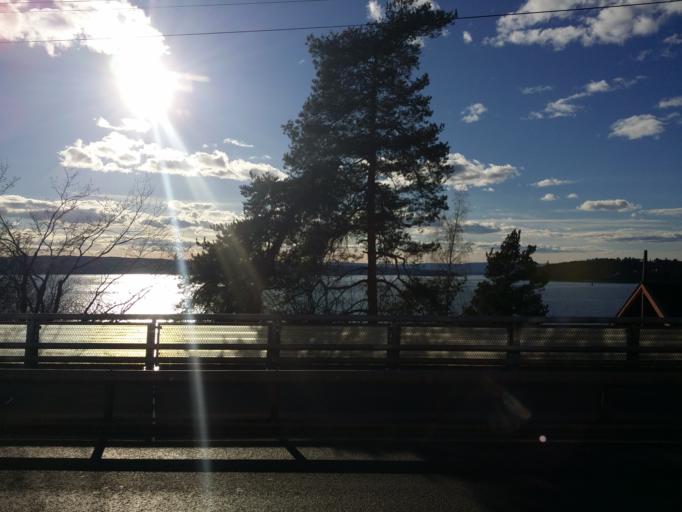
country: NO
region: Akershus
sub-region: Oppegard
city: Kolbotn
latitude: 59.8569
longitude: 10.7849
